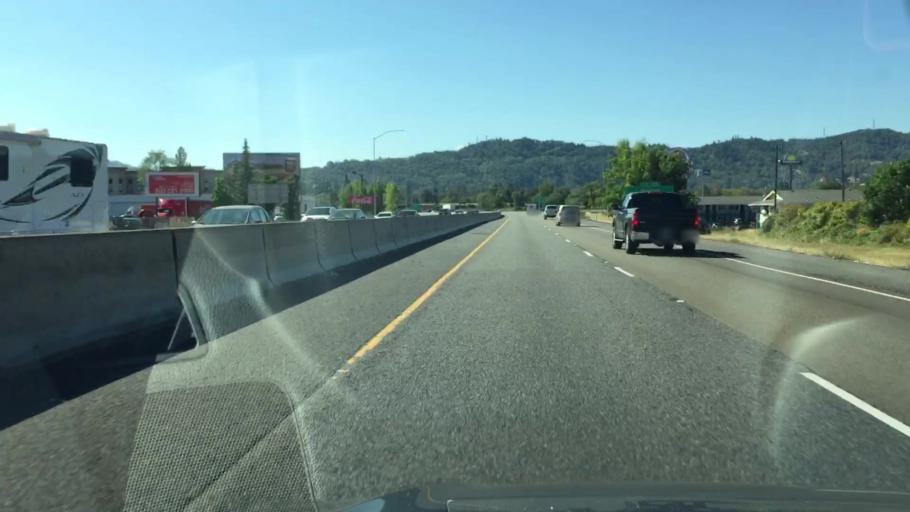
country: US
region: Oregon
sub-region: Douglas County
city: Roseburg
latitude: 43.2324
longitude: -123.3614
